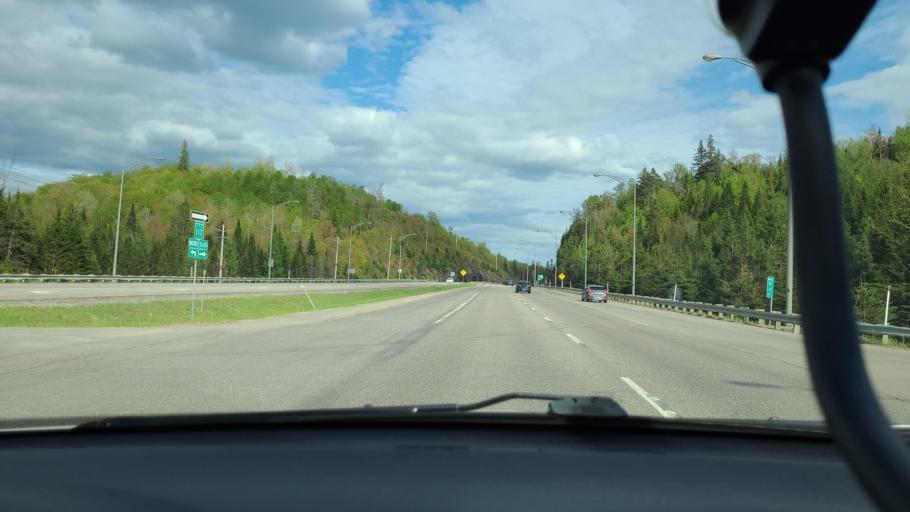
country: CA
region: Quebec
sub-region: Laurentides
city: Sainte-Agathe-des-Monts
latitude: 46.0896
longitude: -74.3310
